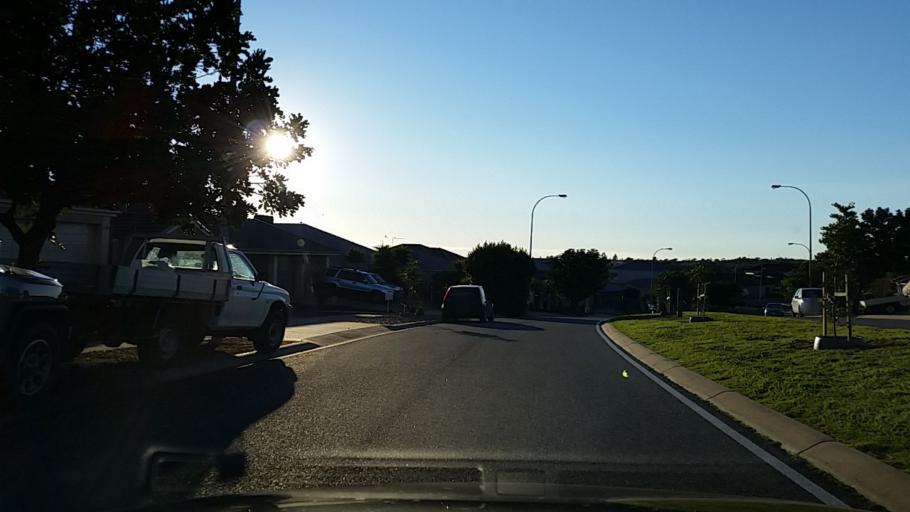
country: AU
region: South Australia
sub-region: Onkaparinga
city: Moana
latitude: -35.2093
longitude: 138.4840
